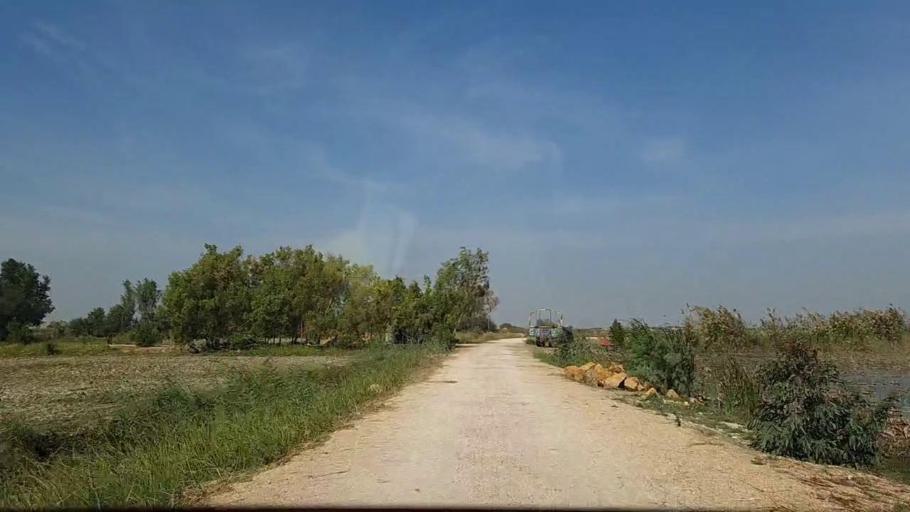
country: PK
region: Sindh
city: Daro Mehar
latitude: 24.7051
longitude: 68.1499
